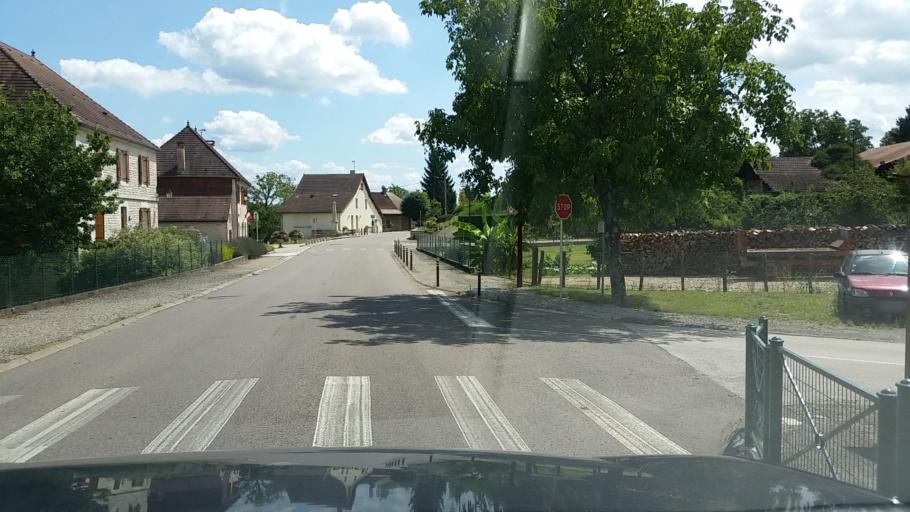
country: FR
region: Franche-Comte
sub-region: Departement du Jura
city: Bletterans
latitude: 46.7628
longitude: 5.4477
